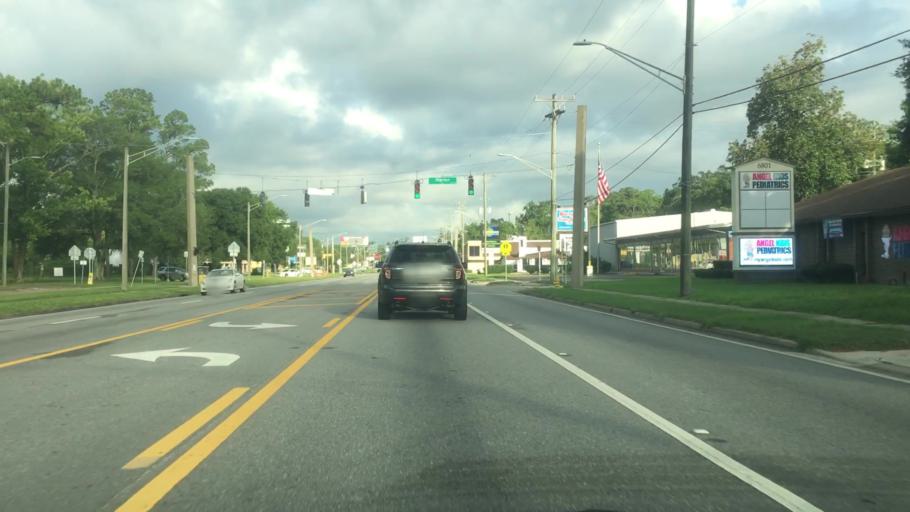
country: US
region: Florida
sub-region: Duval County
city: Jacksonville
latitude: 30.3416
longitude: -81.6032
